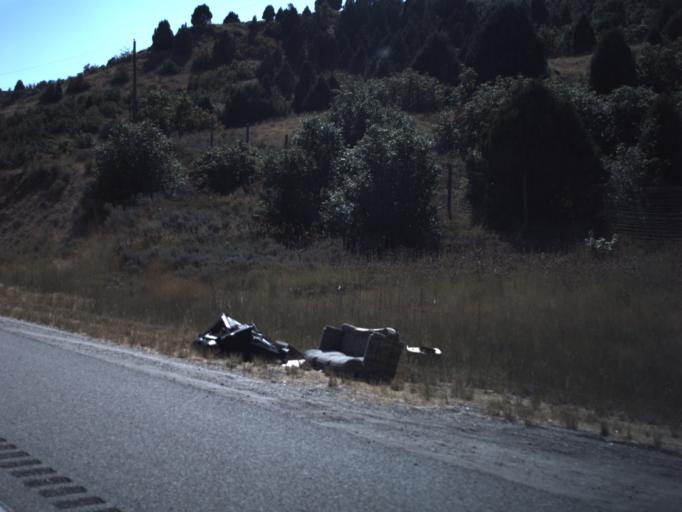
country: US
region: Utah
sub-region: Box Elder County
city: Brigham City
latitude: 41.5371
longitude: -111.9583
